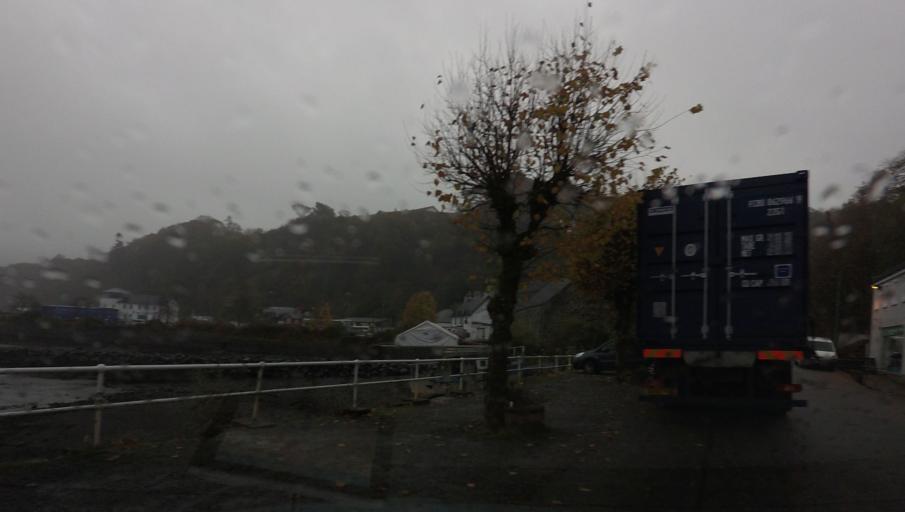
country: GB
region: Scotland
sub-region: Argyll and Bute
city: Isle Of Mull
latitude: 56.6216
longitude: -6.0697
